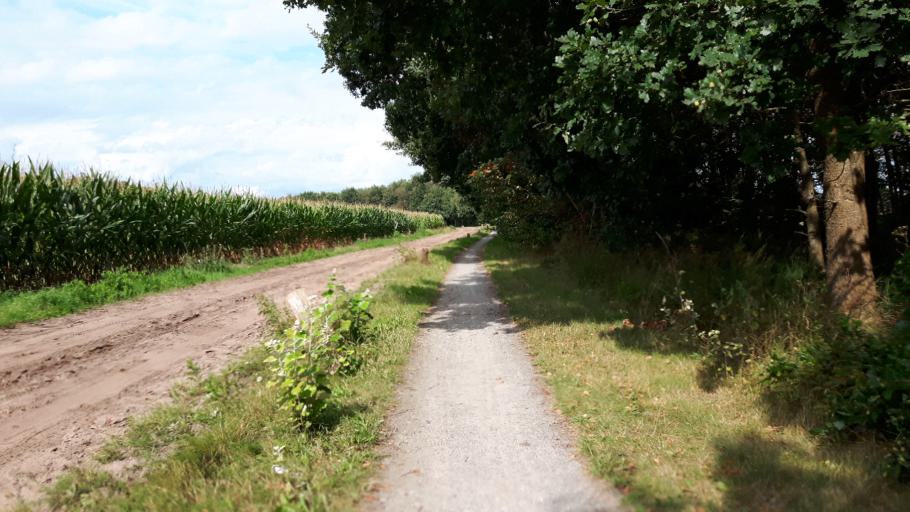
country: NL
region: Groningen
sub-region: Gemeente Leek
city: Leek
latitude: 53.1069
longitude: 6.3996
